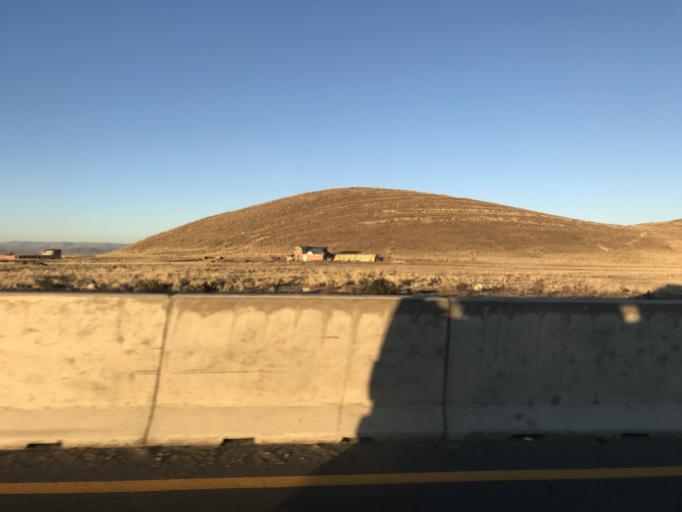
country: BO
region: La Paz
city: Batallas
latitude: -16.3041
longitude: -68.4807
